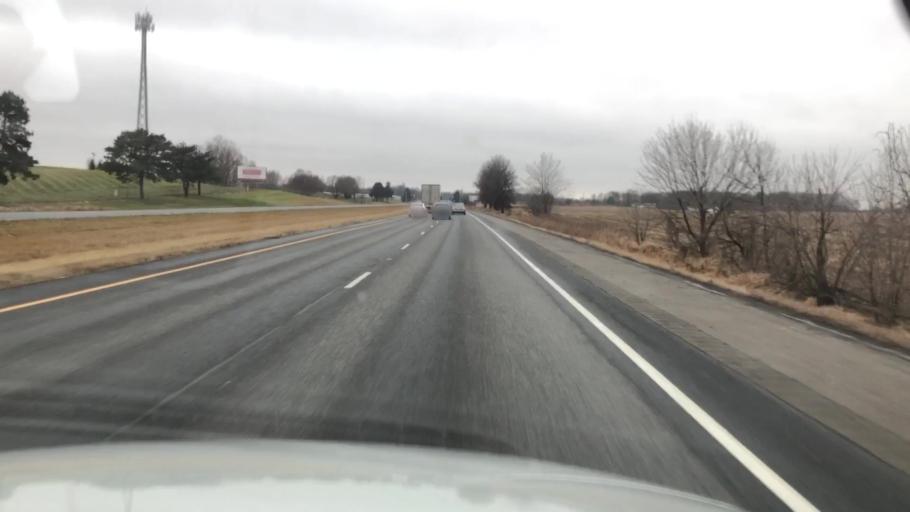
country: US
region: Indiana
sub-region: Whitley County
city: Churubusco
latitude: 41.1267
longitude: -85.3484
